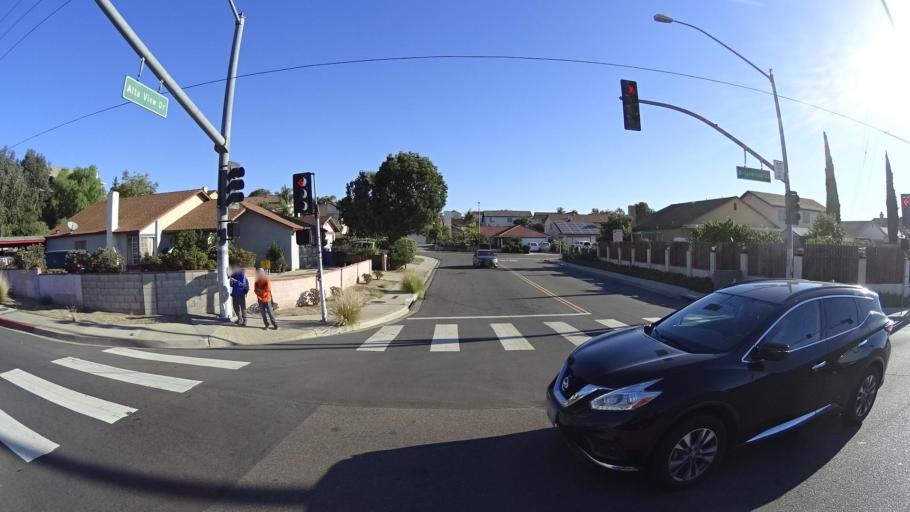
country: US
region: California
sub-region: San Diego County
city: Bonita
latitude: 32.6829
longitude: -117.0318
